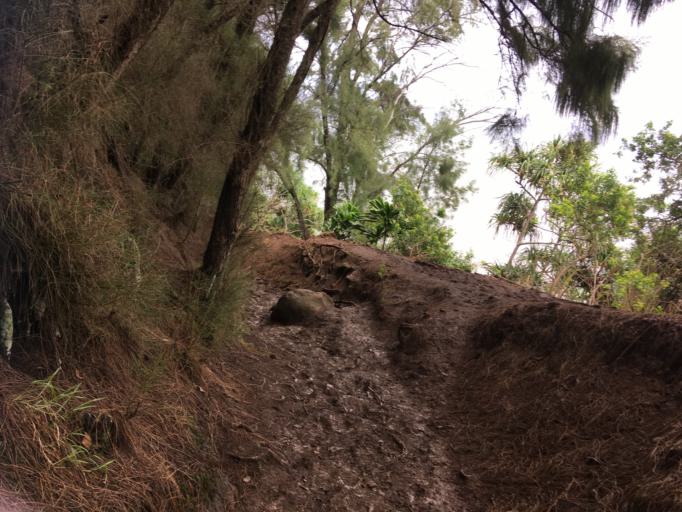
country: US
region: Hawaii
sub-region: Hawaii County
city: Kapaau
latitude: 20.2045
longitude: -155.7327
